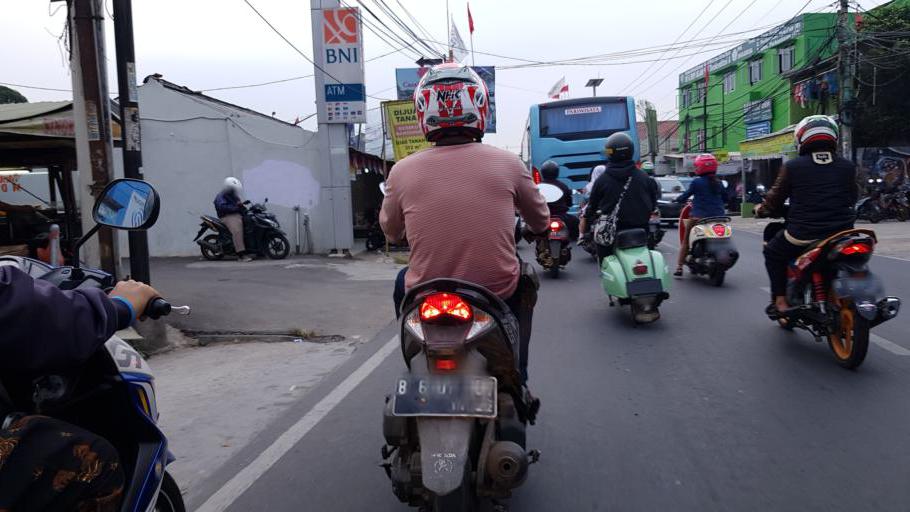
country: ID
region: West Java
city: Sawangan
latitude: -6.3950
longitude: 106.7734
